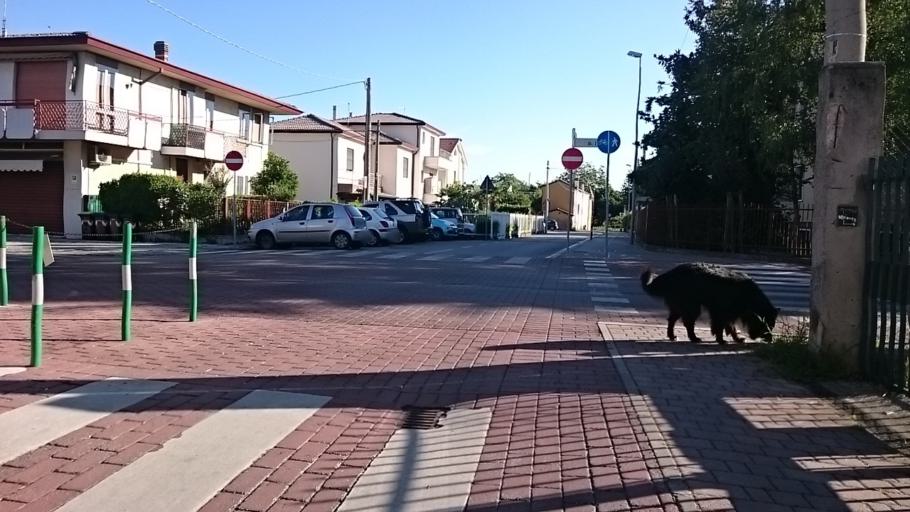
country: IT
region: Veneto
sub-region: Provincia di Padova
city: Mejaniga
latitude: 45.4438
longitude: 11.8971
